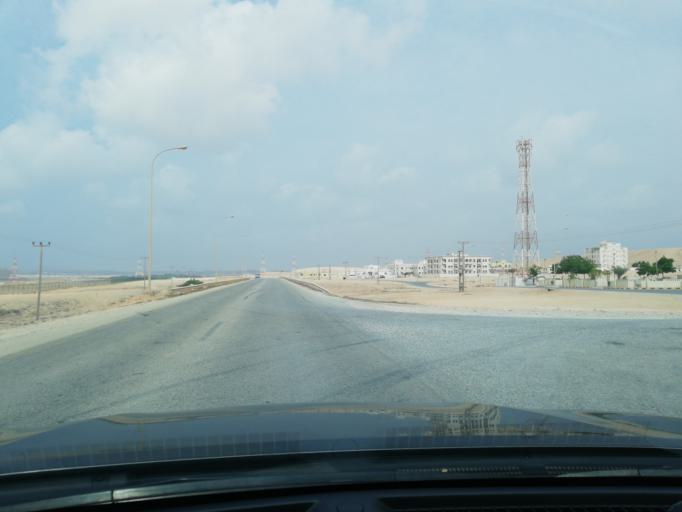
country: OM
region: Zufar
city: Salalah
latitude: 16.9486
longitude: 53.9670
